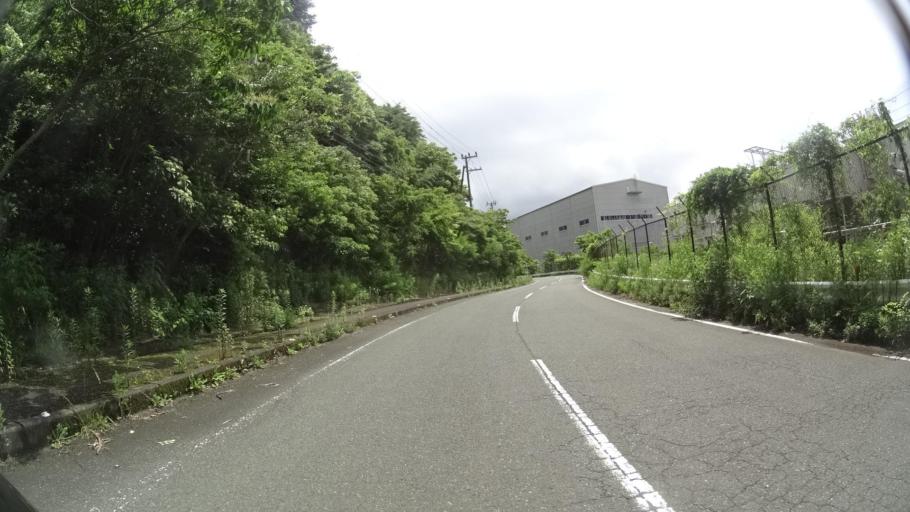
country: JP
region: Kyoto
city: Maizuru
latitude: 35.5308
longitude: 135.3469
